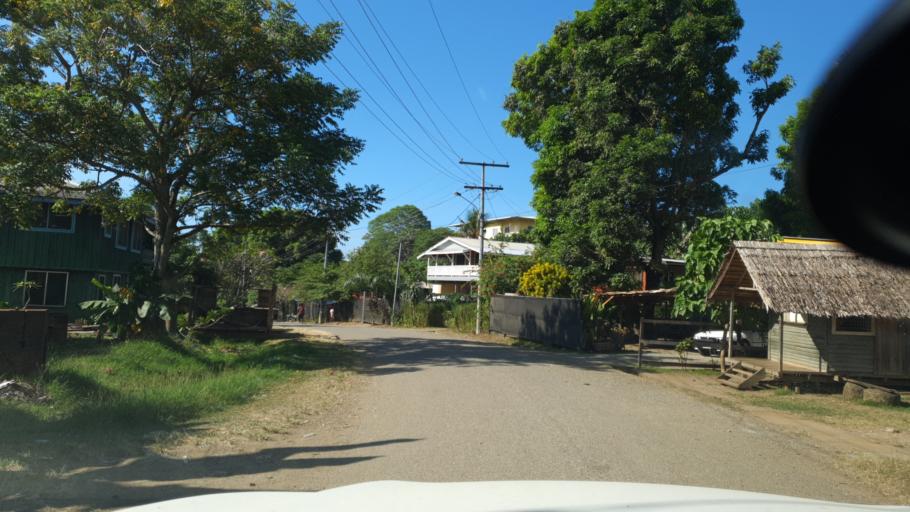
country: SB
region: Guadalcanal
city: Honiara
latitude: -9.4458
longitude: 159.9834
